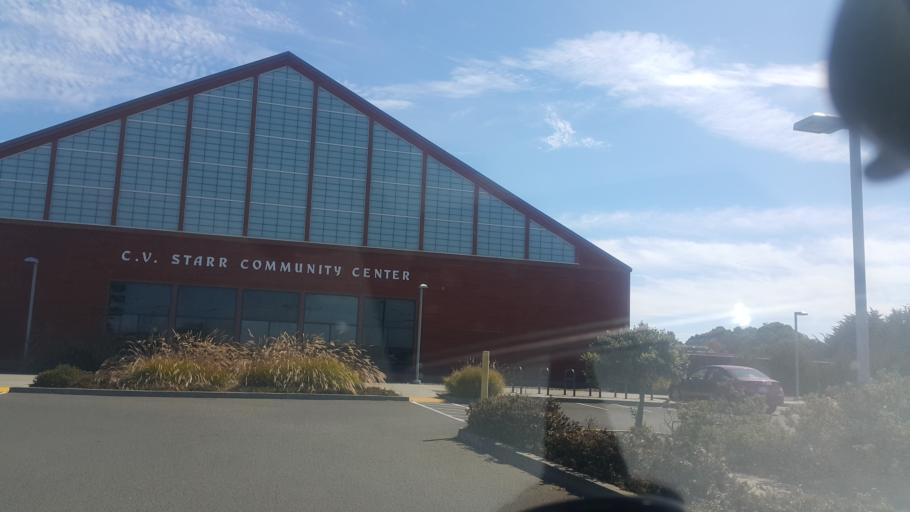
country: US
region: California
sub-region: Mendocino County
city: Fort Bragg
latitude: 39.4391
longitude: -123.7950
